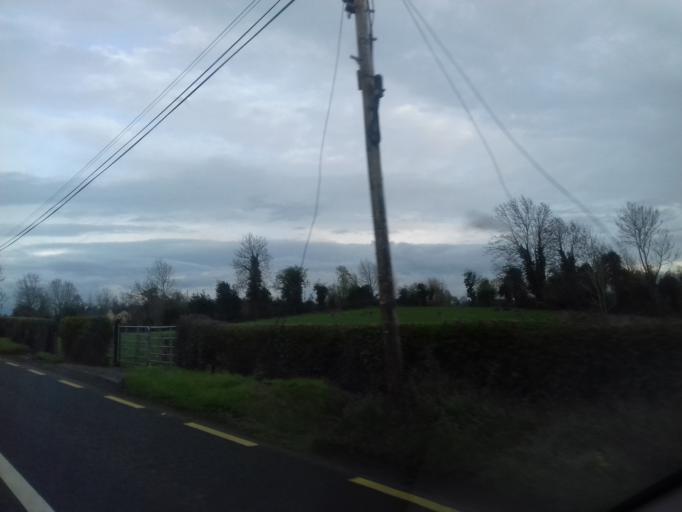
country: IE
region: Ulster
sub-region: An Cabhan
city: Belturbet
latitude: 54.0905
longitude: -7.4907
